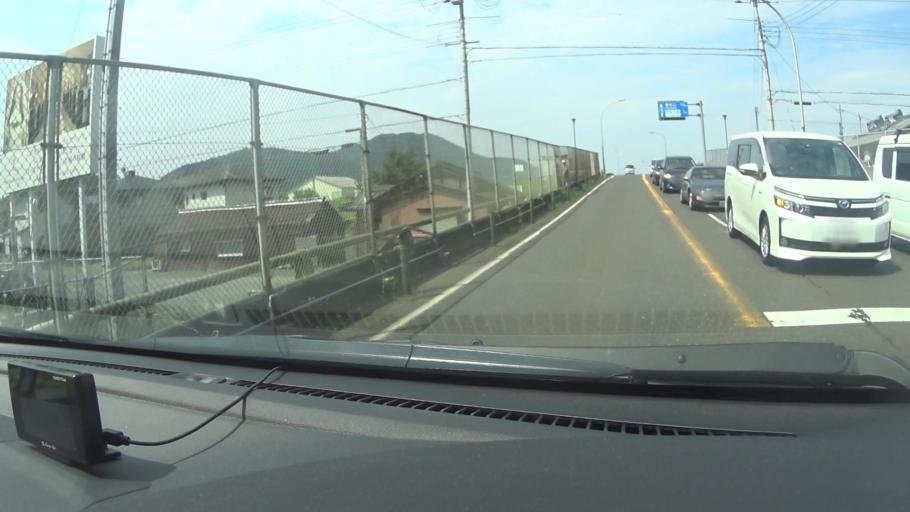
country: JP
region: Kyoto
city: Ayabe
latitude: 35.2992
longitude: 135.2671
